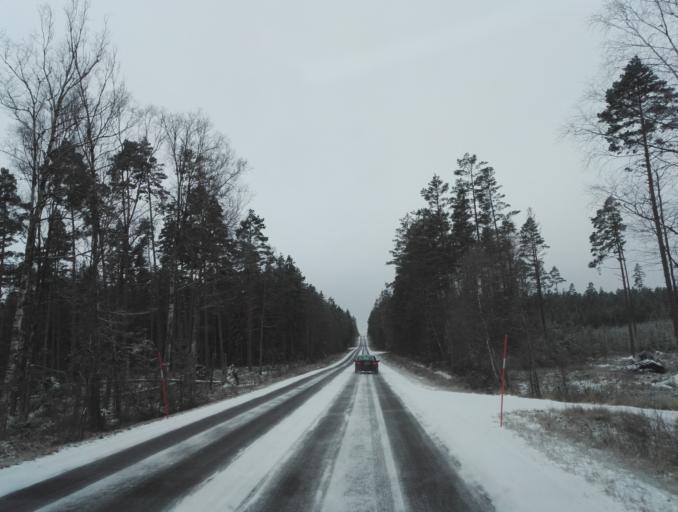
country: SE
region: Kronoberg
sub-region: Lessebo Kommun
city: Lessebo
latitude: 56.7664
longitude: 15.2928
